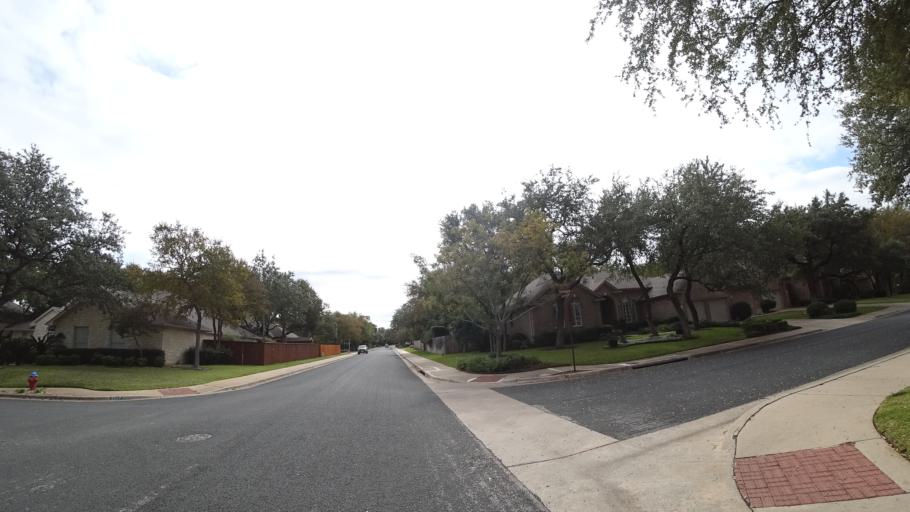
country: US
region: Texas
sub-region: Williamson County
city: Brushy Creek
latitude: 30.5168
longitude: -97.7444
